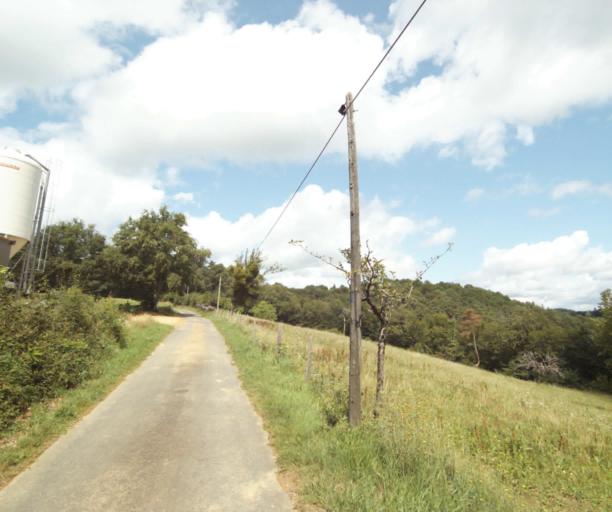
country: FR
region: Limousin
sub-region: Departement de la Correze
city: Sainte-Fortunade
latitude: 45.1950
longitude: 1.8464
